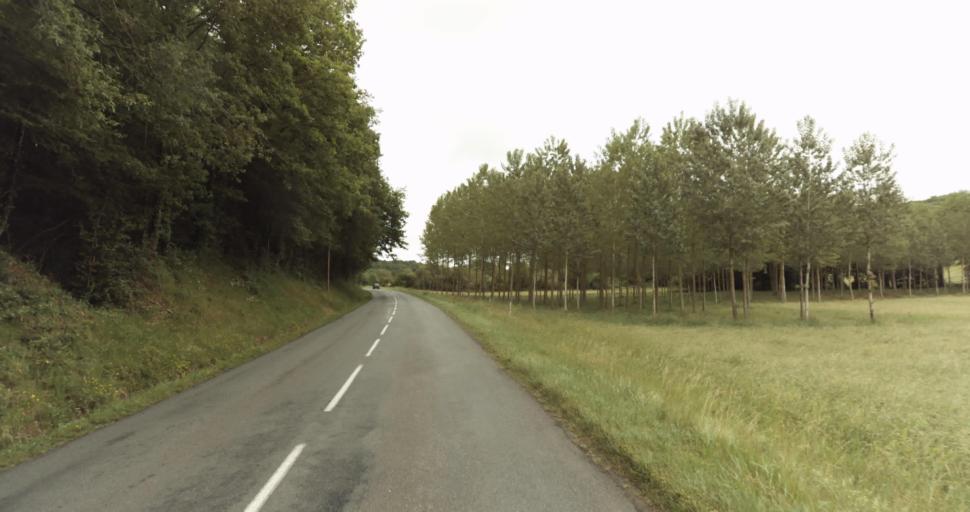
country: FR
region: Aquitaine
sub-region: Departement du Lot-et-Garonne
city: Villereal
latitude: 44.6644
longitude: 0.8759
